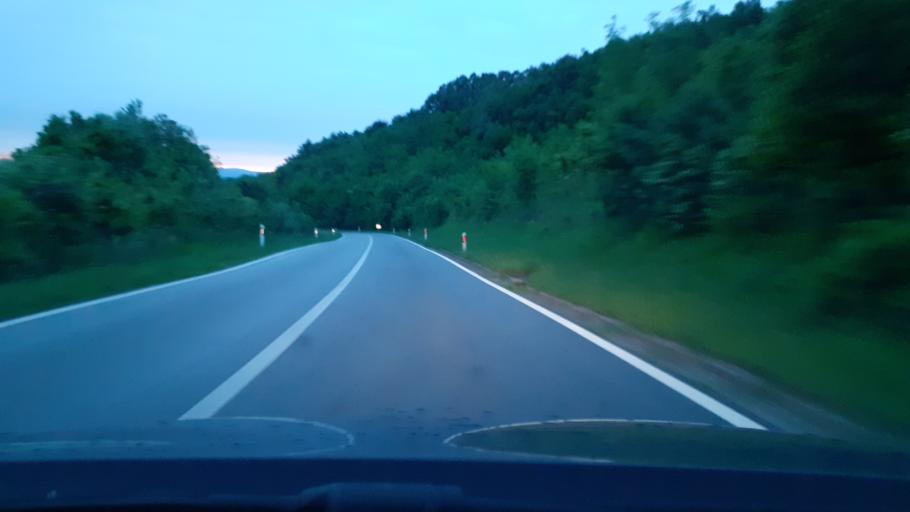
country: HR
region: Pozesko-Slavonska
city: Bilice
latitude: 45.2268
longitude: 17.8509
